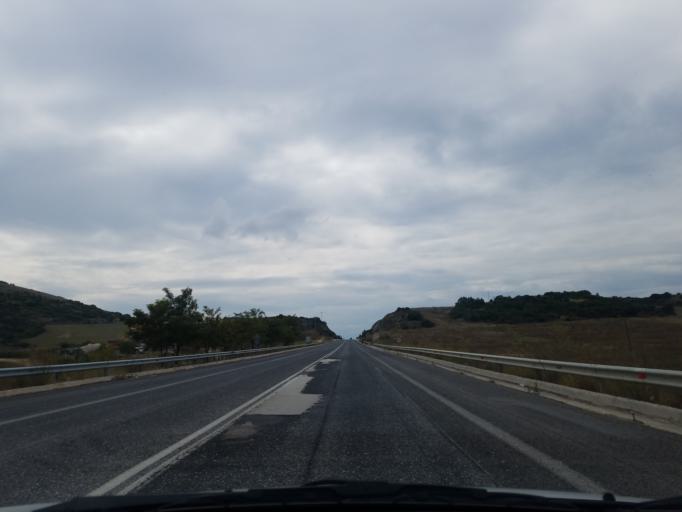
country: GR
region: Central Greece
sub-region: Nomos Fthiotidos
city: Domokos
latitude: 39.1090
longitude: 22.3075
